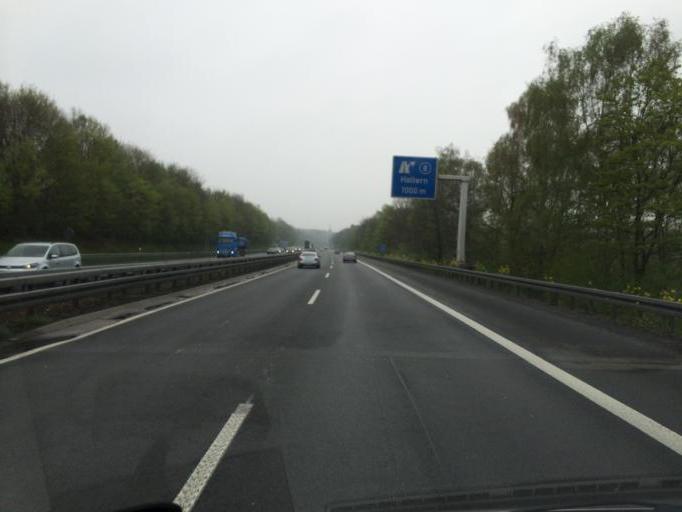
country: DE
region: North Rhine-Westphalia
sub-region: Regierungsbezirk Munster
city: Haltern
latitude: 51.7206
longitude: 7.1510
